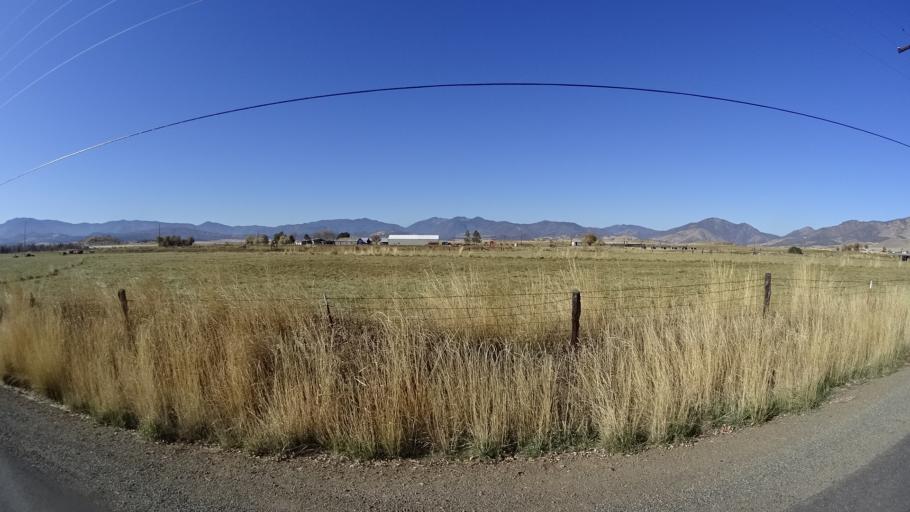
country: US
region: California
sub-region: Siskiyou County
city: Montague
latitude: 41.7407
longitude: -122.5247
